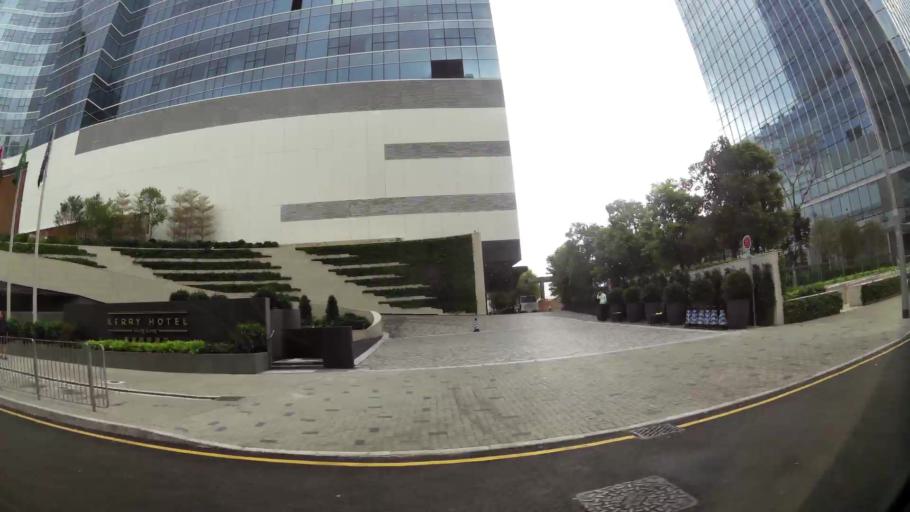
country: HK
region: Kowloon City
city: Kowloon
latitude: 22.3015
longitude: 114.1881
